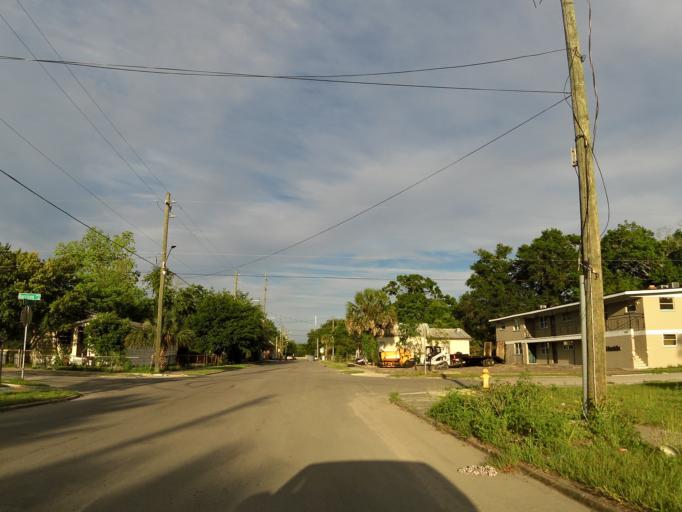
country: US
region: Florida
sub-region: Duval County
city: Jacksonville
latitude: 30.3384
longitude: -81.6405
